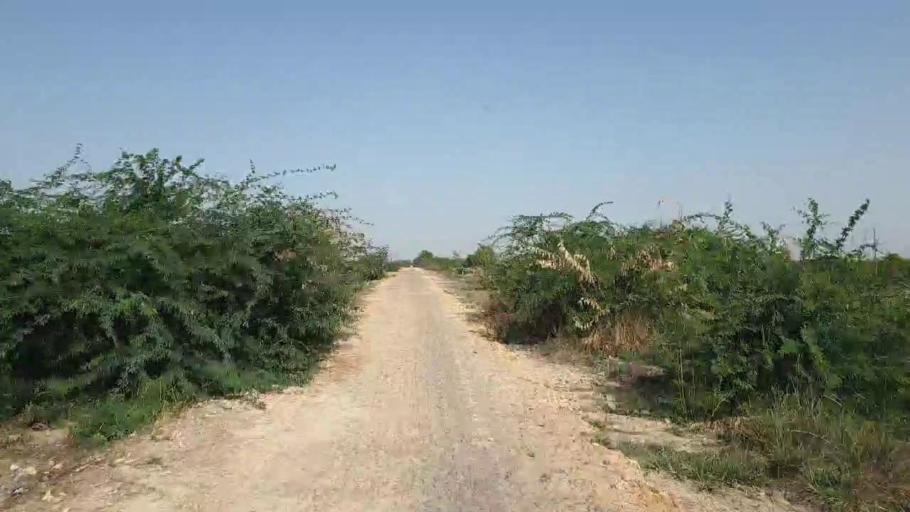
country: PK
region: Sindh
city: Tando Bago
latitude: 24.7219
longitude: 69.0732
